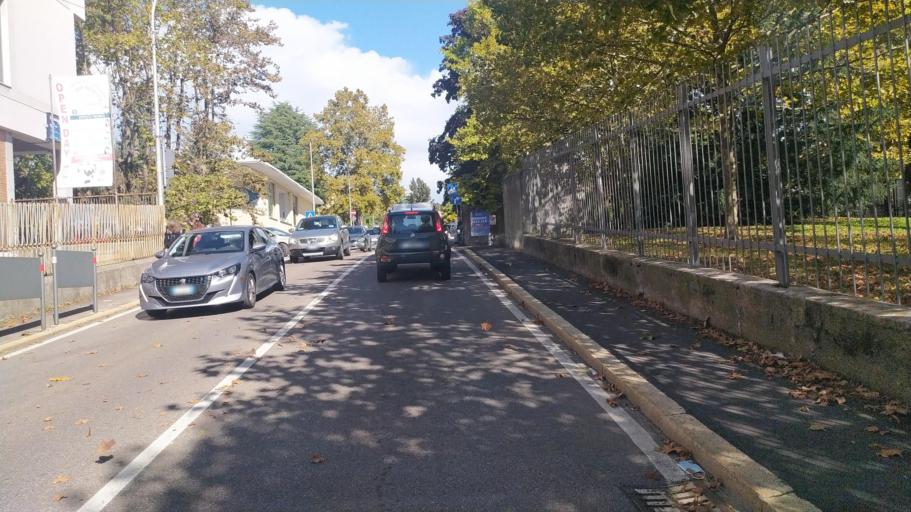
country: IT
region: Lombardy
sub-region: Provincia di Varese
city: Varese
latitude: 45.8170
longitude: 8.8113
